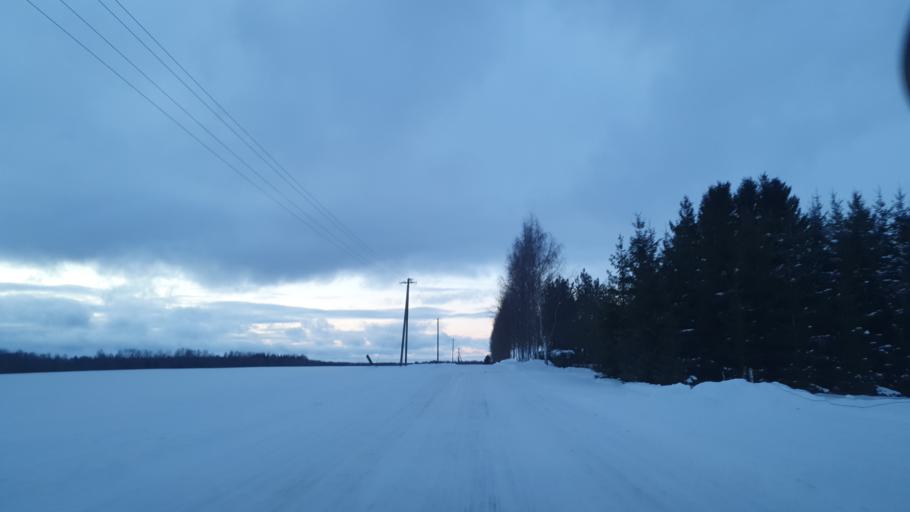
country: EE
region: Jogevamaa
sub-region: Tabivere vald
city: Tabivere
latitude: 58.5780
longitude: 26.5551
